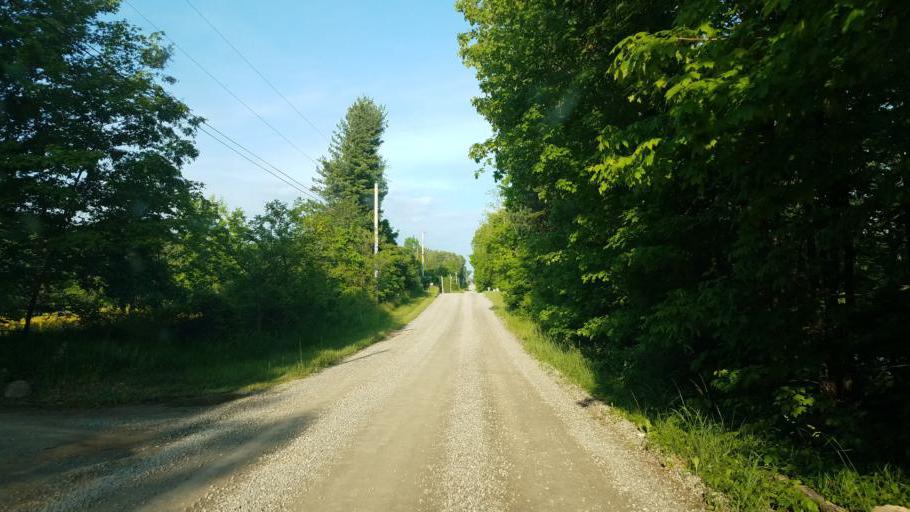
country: US
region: Ohio
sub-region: Morrow County
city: Mount Gilead
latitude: 40.4322
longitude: -82.7665
